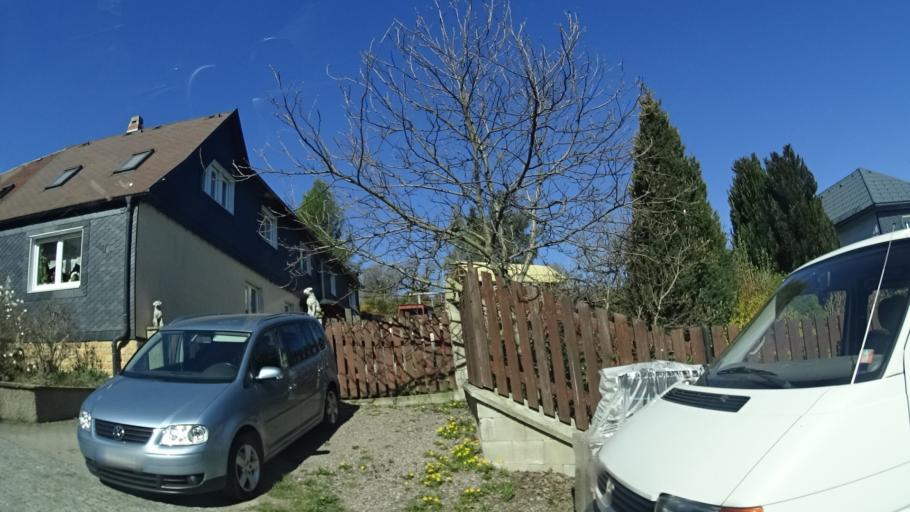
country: DE
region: Thuringia
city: Bohlen
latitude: 50.6009
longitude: 11.0502
